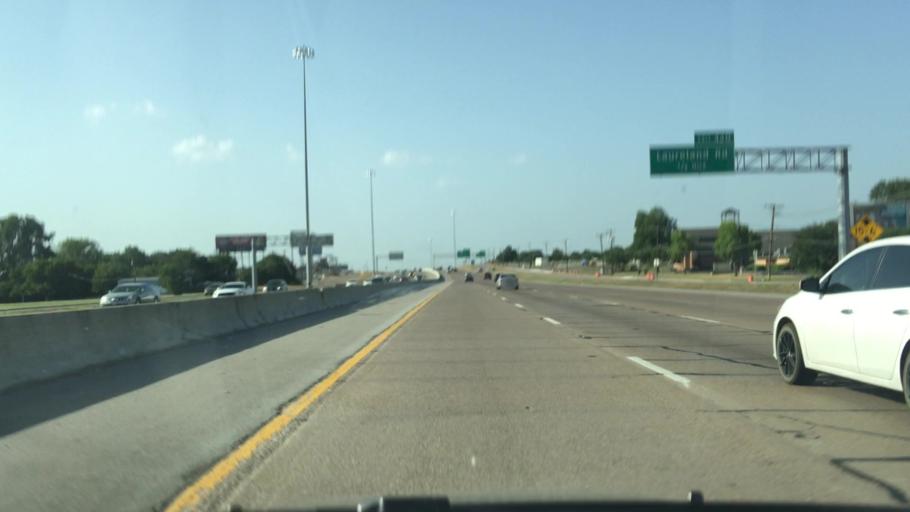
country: US
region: Texas
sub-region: Dallas County
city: DeSoto
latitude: 32.6675
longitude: -96.8228
